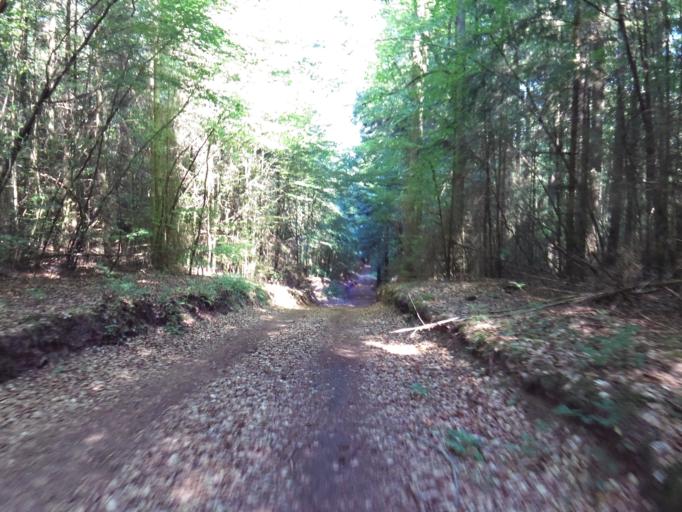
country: DE
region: Rheinland-Pfalz
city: Elmstein
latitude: 49.3843
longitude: 7.9512
